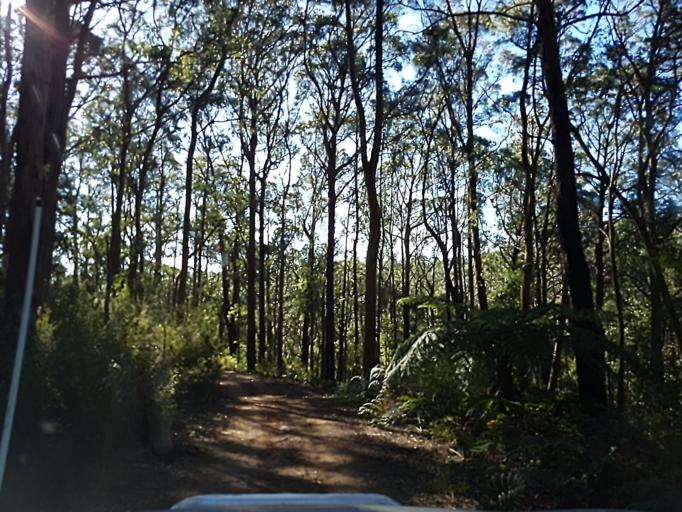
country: AU
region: Victoria
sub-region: Yarra Ranges
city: Healesville
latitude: -37.5641
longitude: 145.4932
